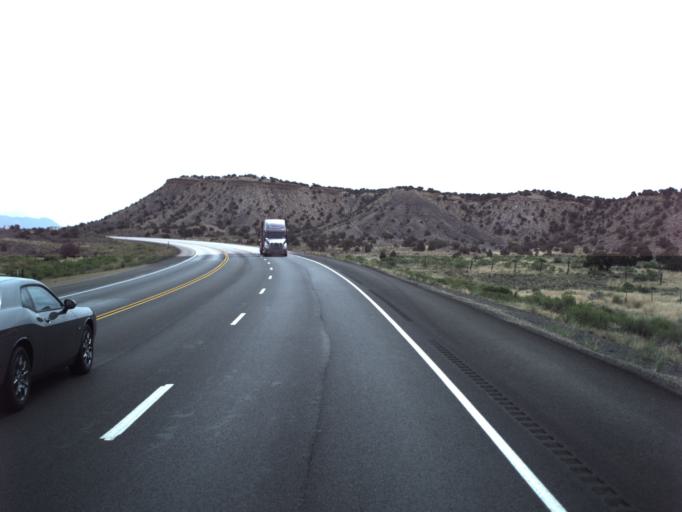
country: US
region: Utah
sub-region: Carbon County
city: Wellington
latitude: 39.5478
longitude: -110.6486
